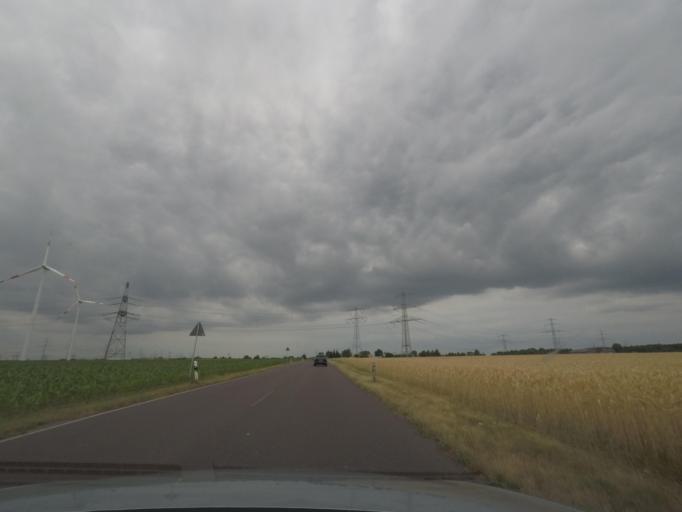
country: DE
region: Saxony-Anhalt
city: Zielitz
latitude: 52.2759
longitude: 11.6480
